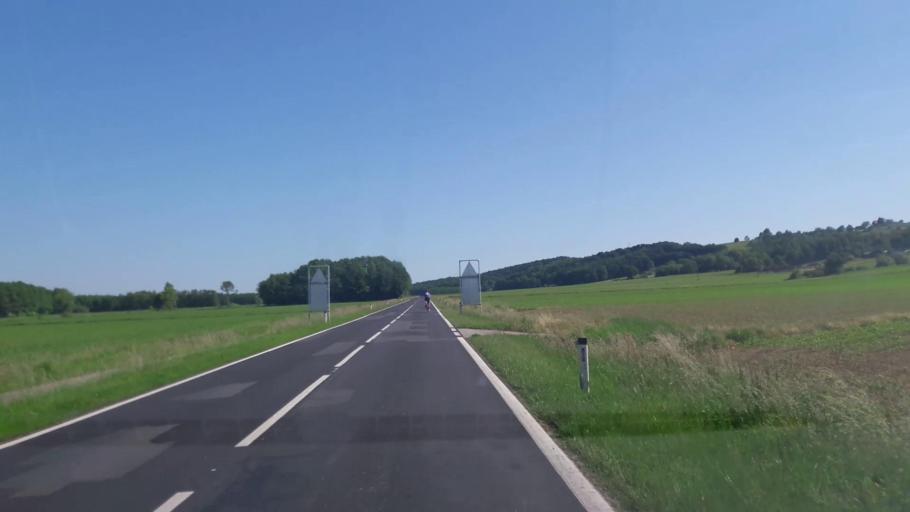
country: AT
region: Burgenland
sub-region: Politischer Bezirk Jennersdorf
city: Deutsch Kaltenbrunn
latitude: 47.0962
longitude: 16.1067
